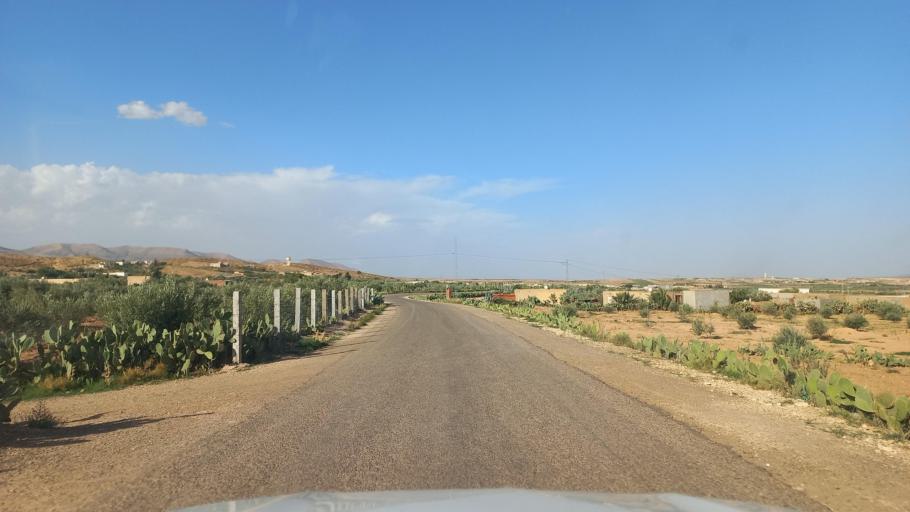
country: TN
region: Al Qasrayn
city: Sbiba
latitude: 35.3756
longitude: 9.0160
